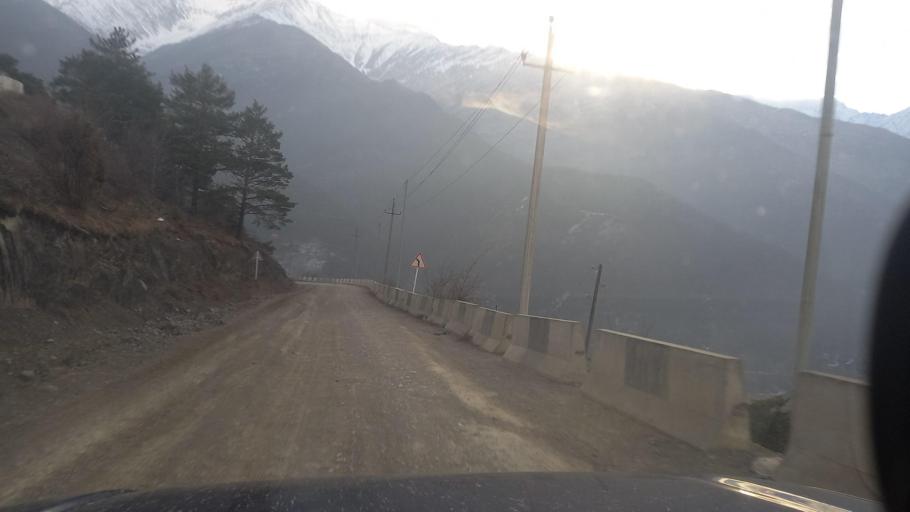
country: RU
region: Ingushetiya
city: Dzhayrakh
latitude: 42.8237
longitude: 44.7051
